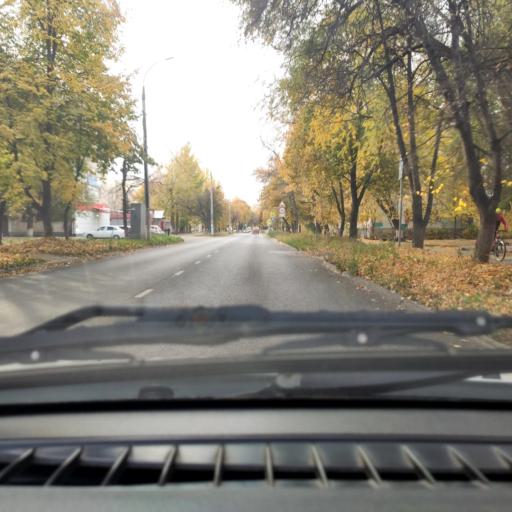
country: RU
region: Samara
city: Tol'yatti
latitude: 53.5047
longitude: 49.4054
